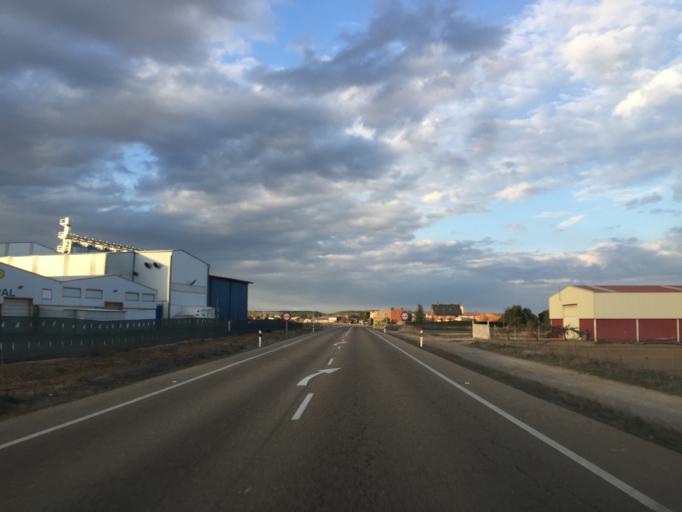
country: ES
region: Castille and Leon
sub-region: Provincia de Palencia
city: Soto de Cerrato
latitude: 41.9770
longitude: -4.4347
